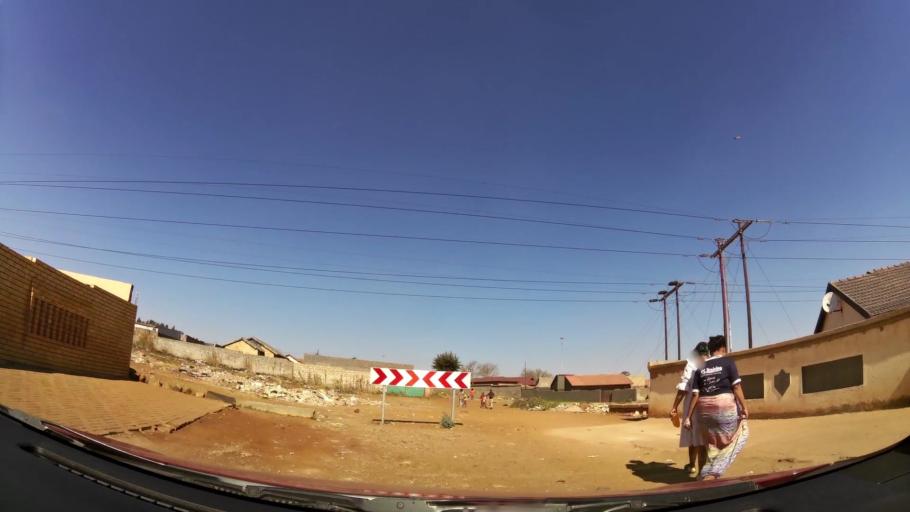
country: ZA
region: Gauteng
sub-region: City of Johannesburg Metropolitan Municipality
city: Soweto
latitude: -26.2365
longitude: 27.8219
